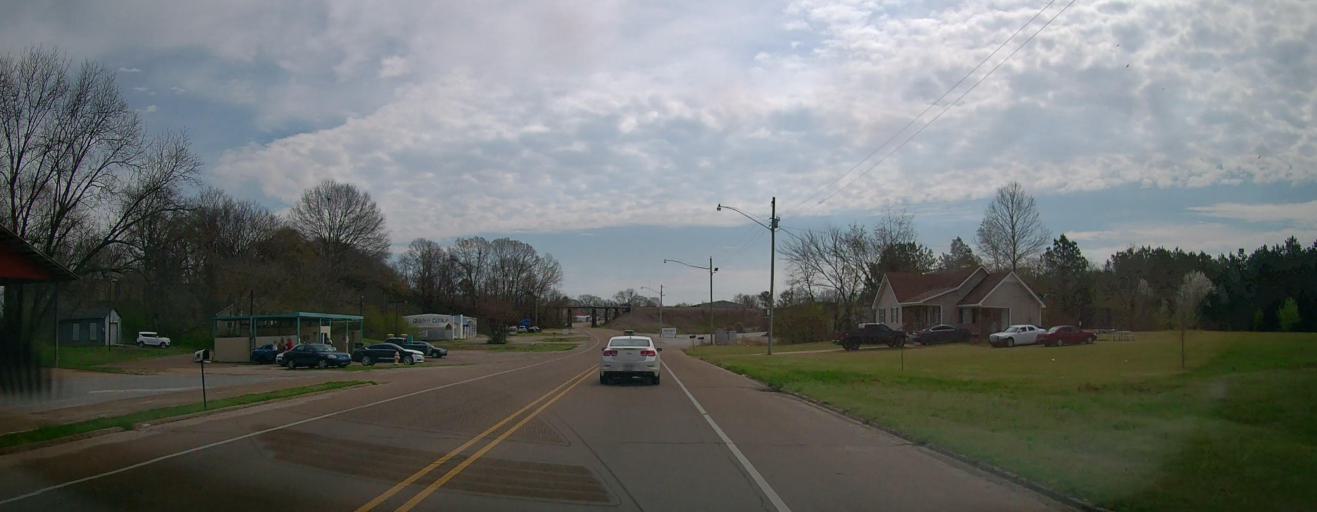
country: US
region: Mississippi
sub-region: Marshall County
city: Holly Springs
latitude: 34.7671
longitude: -89.4364
